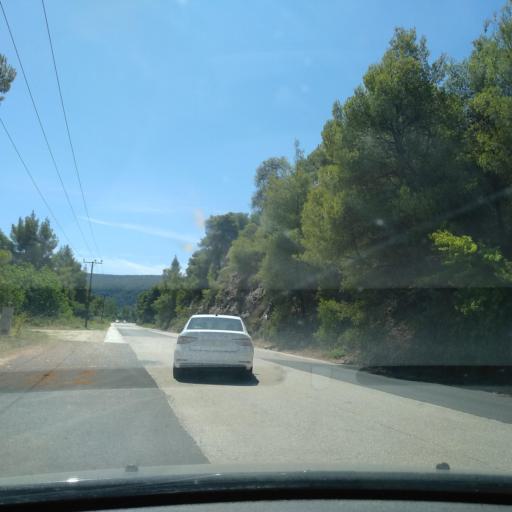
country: GR
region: Central Macedonia
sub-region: Nomos Chalkidikis
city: Agios Nikolaos
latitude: 40.2004
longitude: 23.7649
